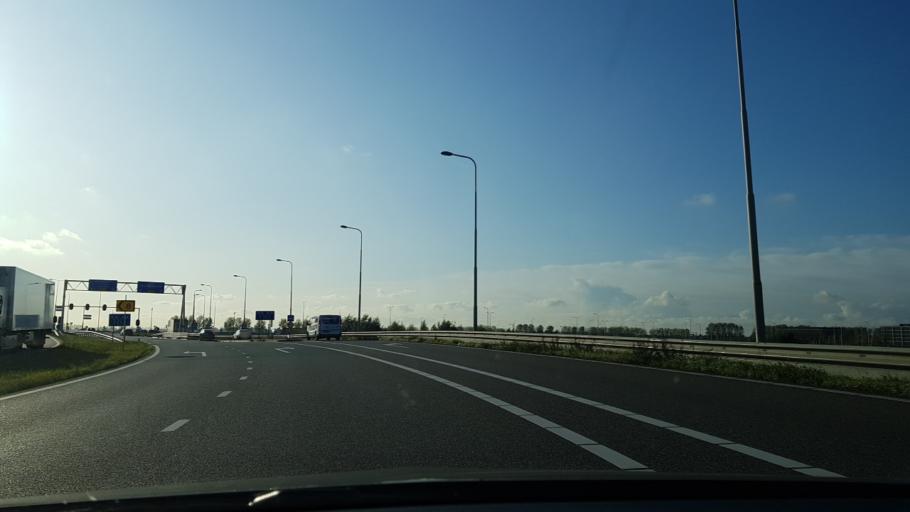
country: NL
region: North Holland
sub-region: Gemeente Haarlemmermeer
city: Hoofddorp
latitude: 52.2860
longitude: 4.7195
